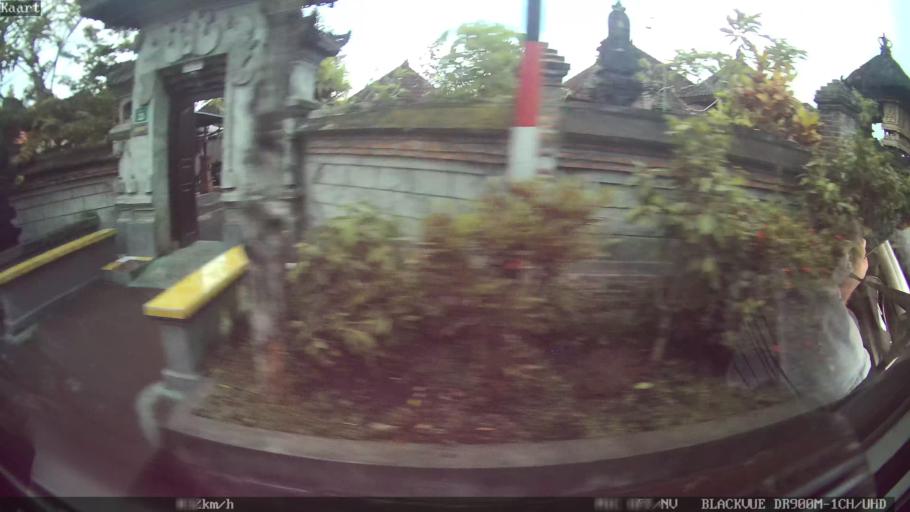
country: ID
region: Bali
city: Banjar Mambalkajanan
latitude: -8.5538
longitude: 115.2104
